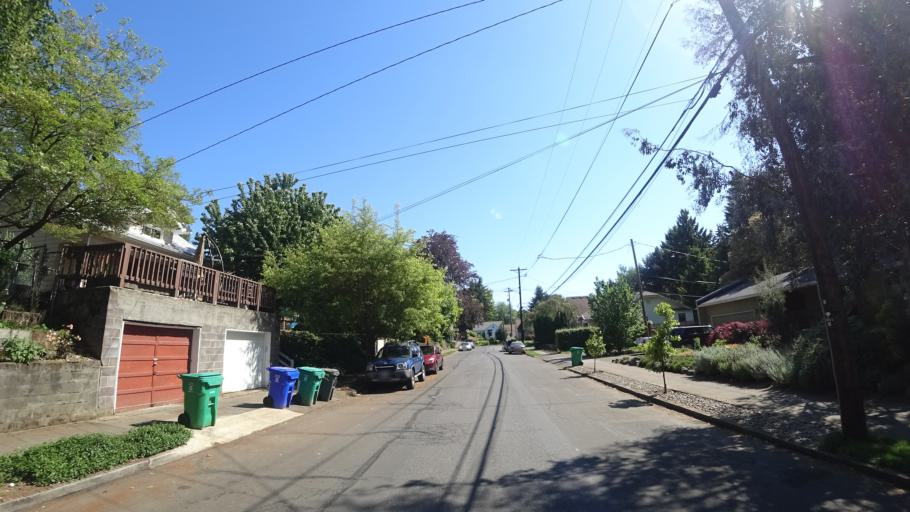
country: US
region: Oregon
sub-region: Clackamas County
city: Milwaukie
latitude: 45.4956
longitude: -122.6208
